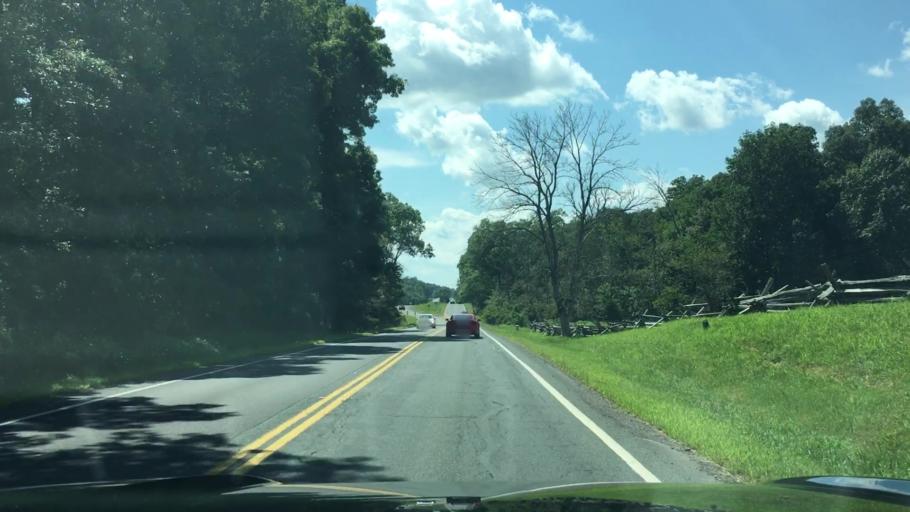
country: US
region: Virginia
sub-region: Prince William County
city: Bull Run
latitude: 38.8106
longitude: -77.5574
